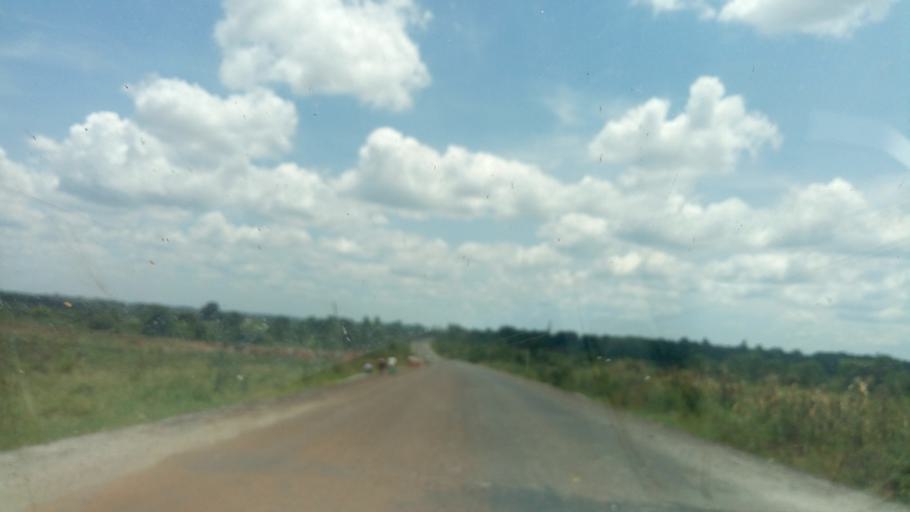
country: UG
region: Western Region
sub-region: Kiryandongo District
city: Kiryandongo
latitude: 1.7901
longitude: 31.9369
